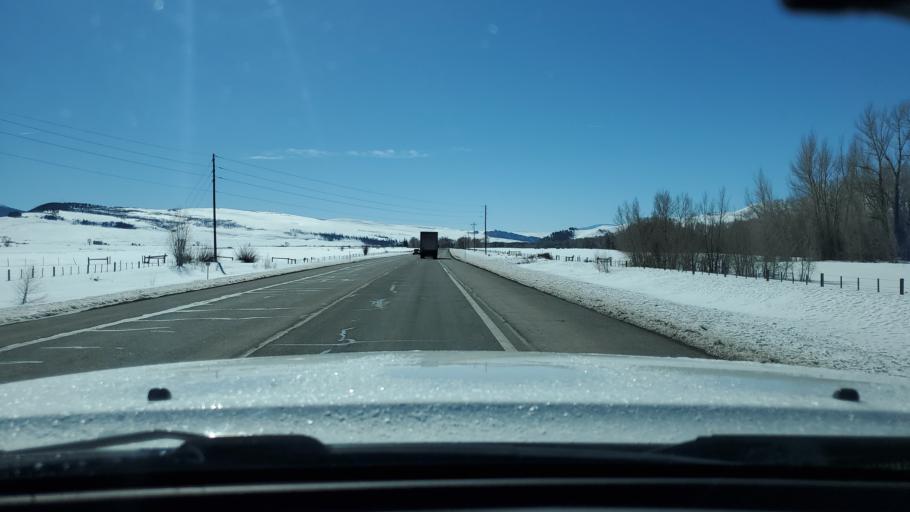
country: US
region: Colorado
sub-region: Gunnison County
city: Crested Butte
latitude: 38.7586
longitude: -106.8623
